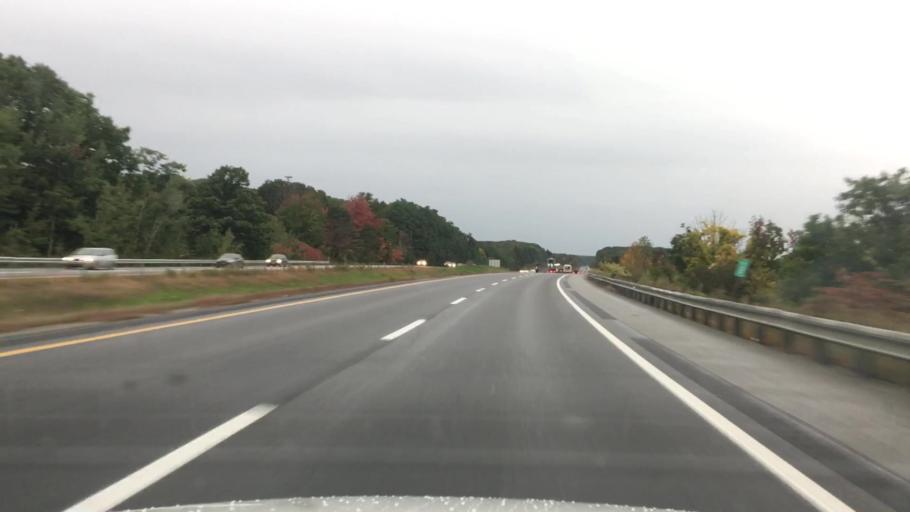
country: US
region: Maine
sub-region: Cumberland County
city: Portland
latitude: 43.6943
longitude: -70.2565
